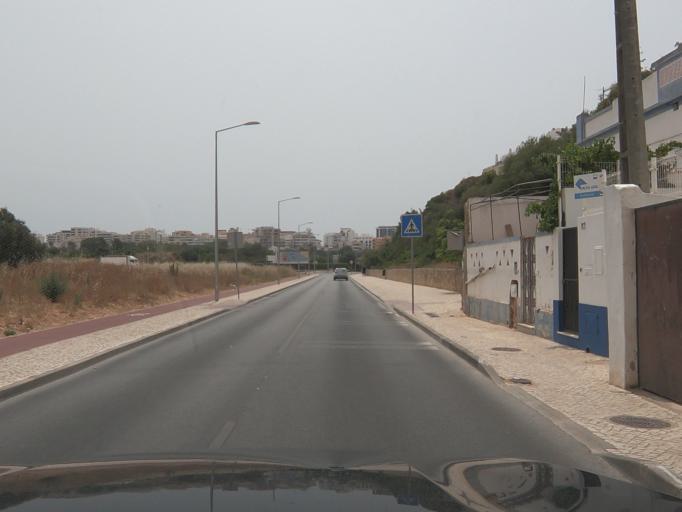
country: PT
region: Faro
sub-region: Portimao
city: Portimao
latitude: 37.1257
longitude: -8.5346
